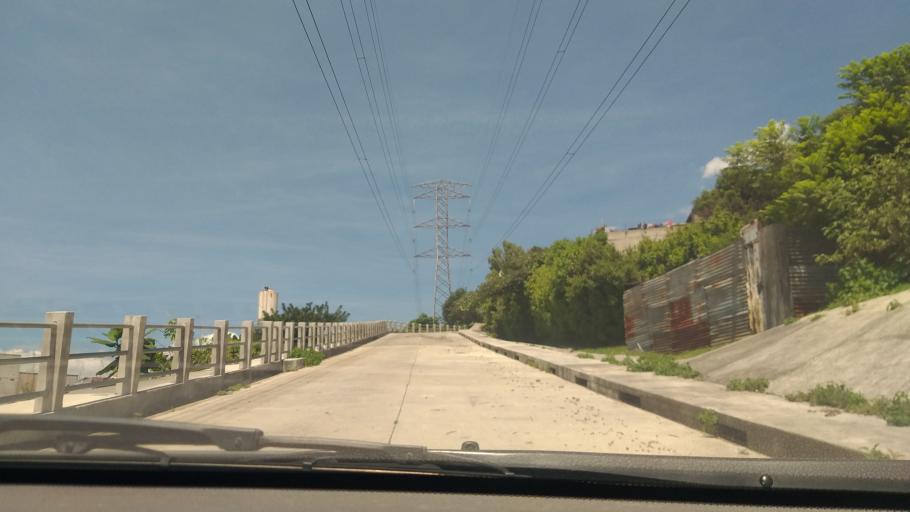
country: GT
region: Guatemala
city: Petapa
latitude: 14.5387
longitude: -90.5511
